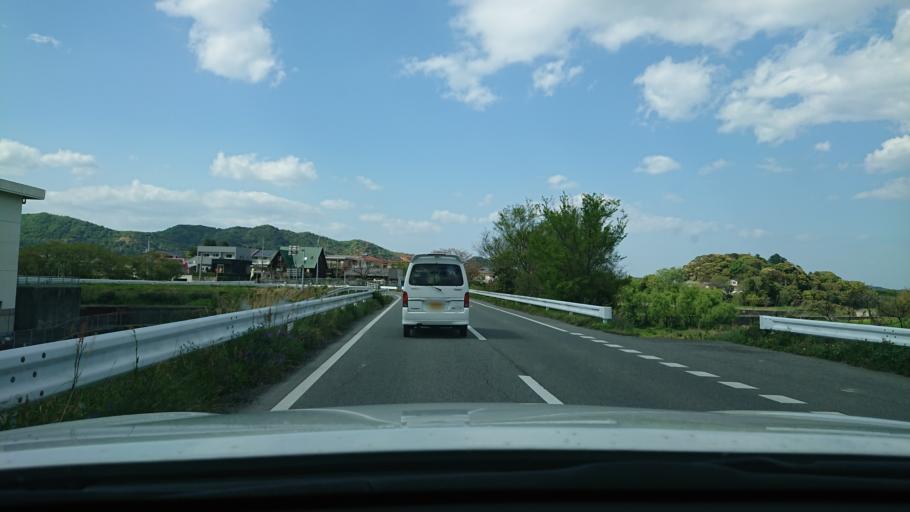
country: JP
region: Tokushima
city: Komatsushimacho
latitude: 33.9995
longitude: 134.5475
